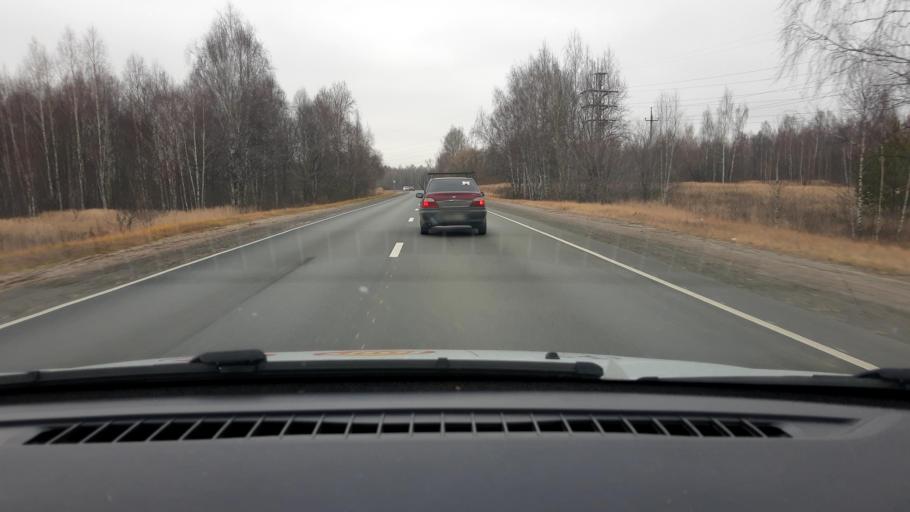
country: RU
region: Nizjnij Novgorod
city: Gorodets
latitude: 56.5834
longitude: 43.4710
